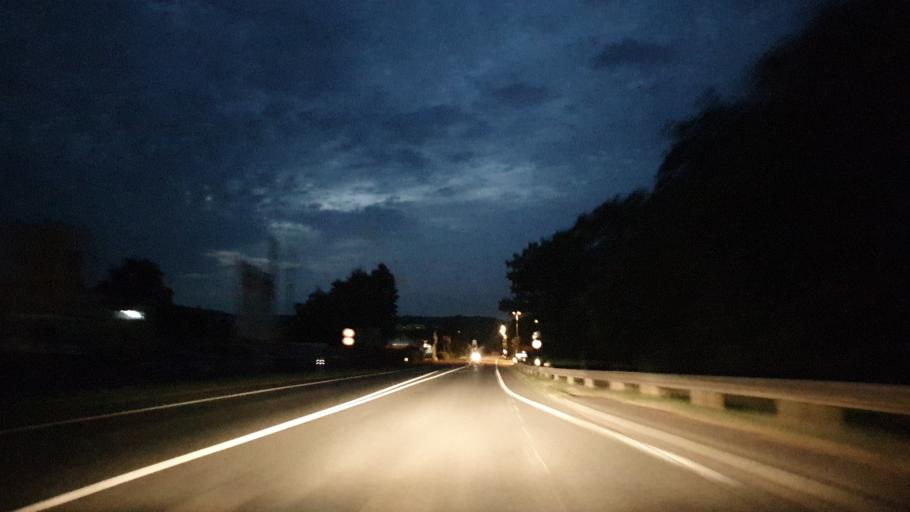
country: DE
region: Rheinland-Pfalz
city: Andernach
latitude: 50.4174
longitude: 7.4093
